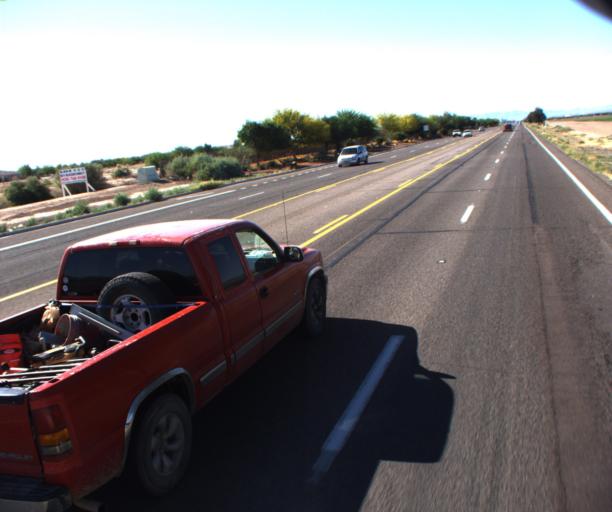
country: US
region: Arizona
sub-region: Mohave County
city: Mohave Valley
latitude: 34.9637
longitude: -114.5980
